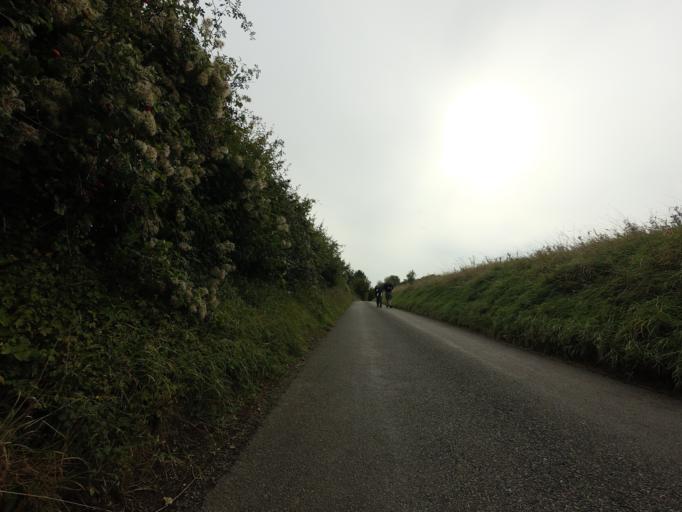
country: GB
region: England
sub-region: Hertfordshire
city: Reed
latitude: 51.9823
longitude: 0.0397
